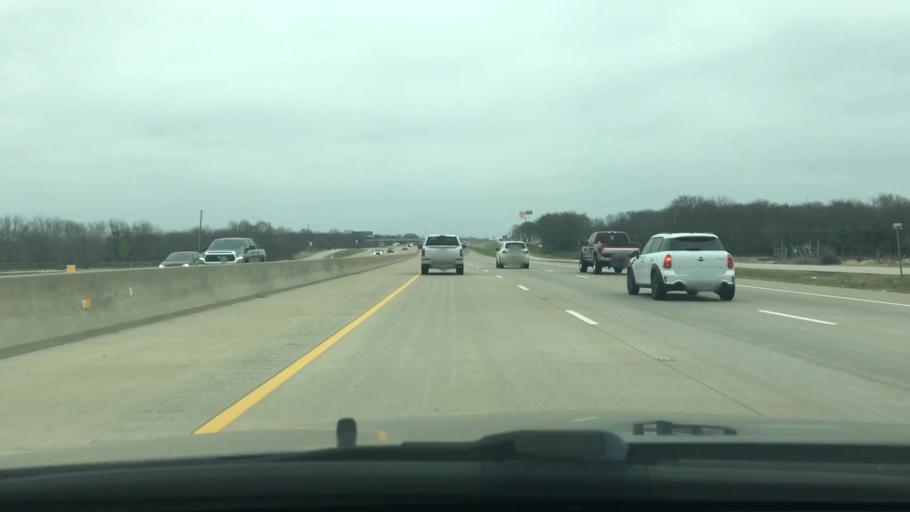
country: US
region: Texas
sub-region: Ellis County
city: Ennis
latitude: 32.2499
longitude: -96.4997
